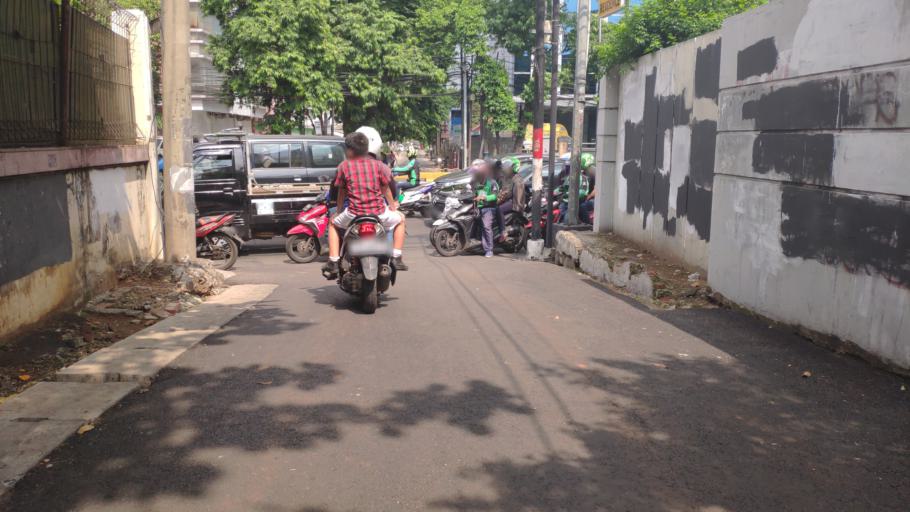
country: ID
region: Jakarta Raya
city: Jakarta
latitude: -6.2611
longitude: 106.8289
